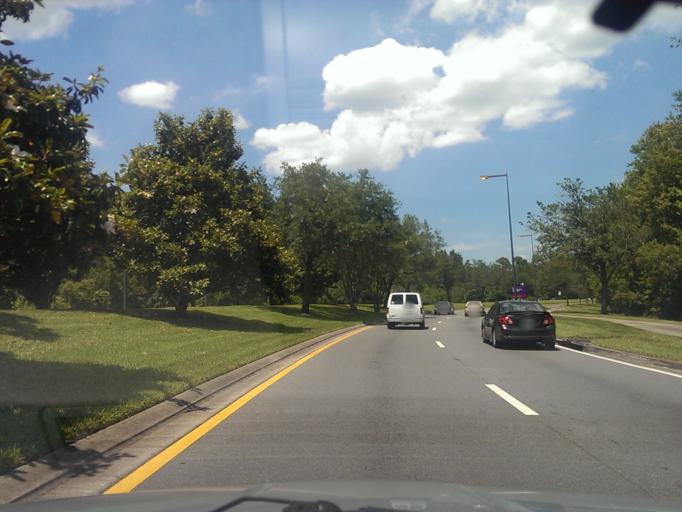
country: US
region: Florida
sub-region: Osceola County
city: Celebration
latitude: 28.3521
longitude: -81.5778
